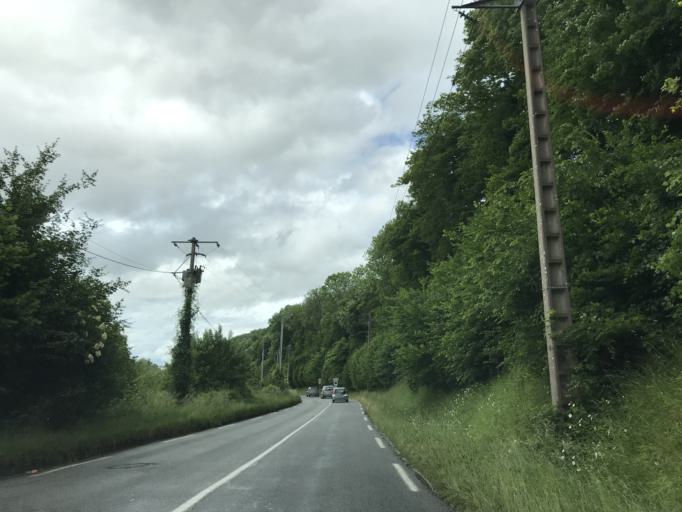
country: FR
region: Haute-Normandie
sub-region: Departement de l'Eure
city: Arnieres-sur-Iton
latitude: 49.0076
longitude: 1.1152
